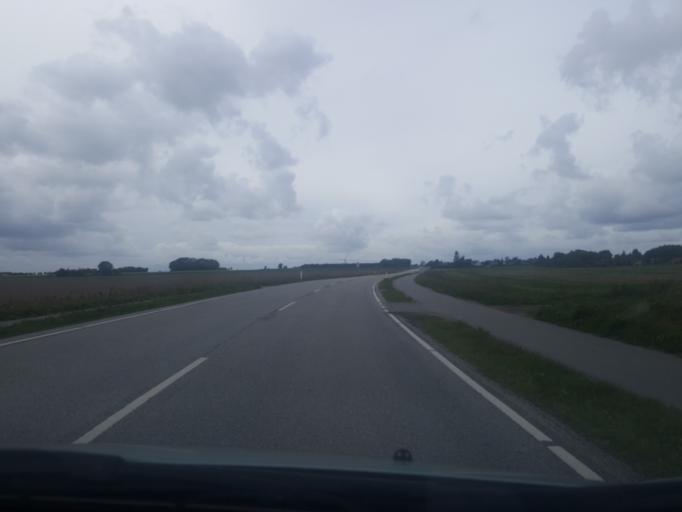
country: DK
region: Zealand
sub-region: Guldborgsund Kommune
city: Nykobing Falster
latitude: 54.7019
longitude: 11.9318
